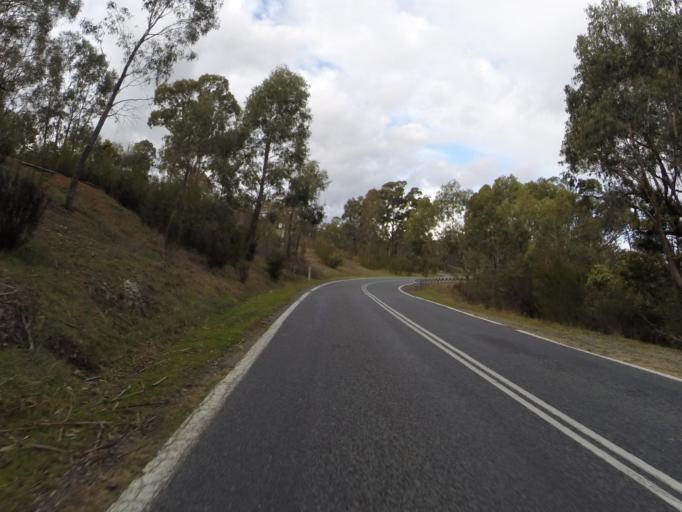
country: AU
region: Australian Capital Territory
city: Macquarie
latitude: -35.3257
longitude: 148.9423
